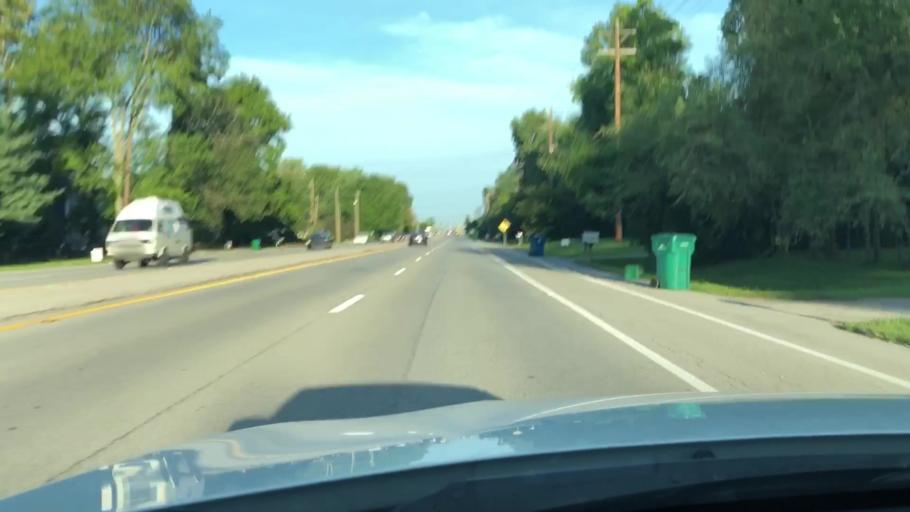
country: US
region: Kentucky
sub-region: Jefferson County
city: Saint Regis Park
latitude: 38.2194
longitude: -85.6138
